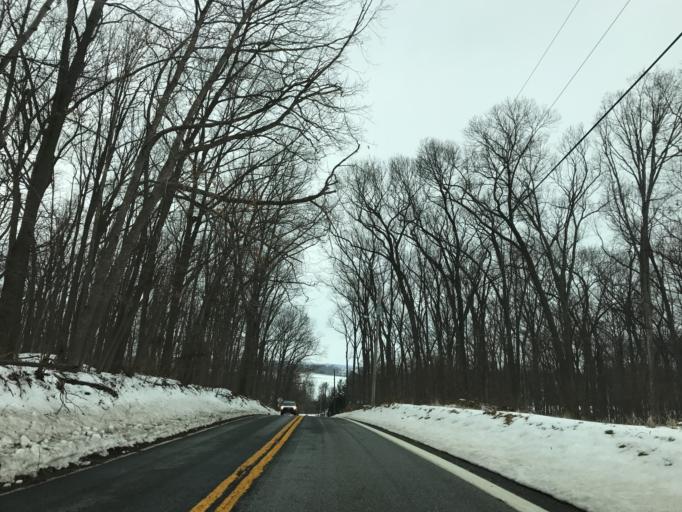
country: US
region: Pennsylvania
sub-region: York County
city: Susquehanna Trails
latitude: 39.7117
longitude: -76.4280
